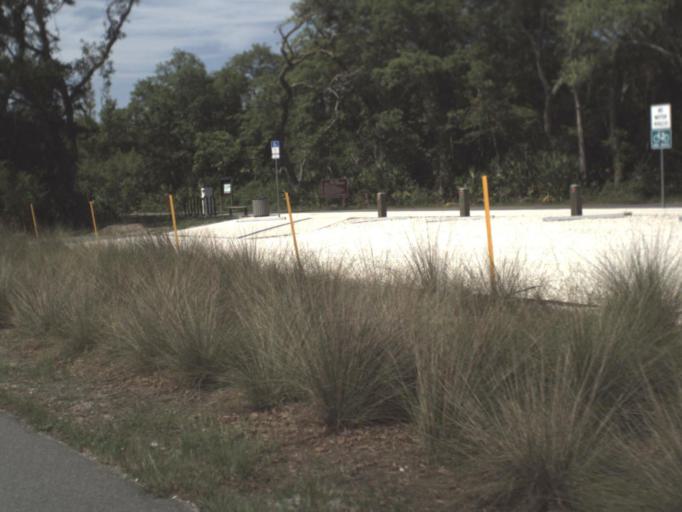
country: US
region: Florida
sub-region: Duval County
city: Atlantic Beach
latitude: 30.4689
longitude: -81.4396
